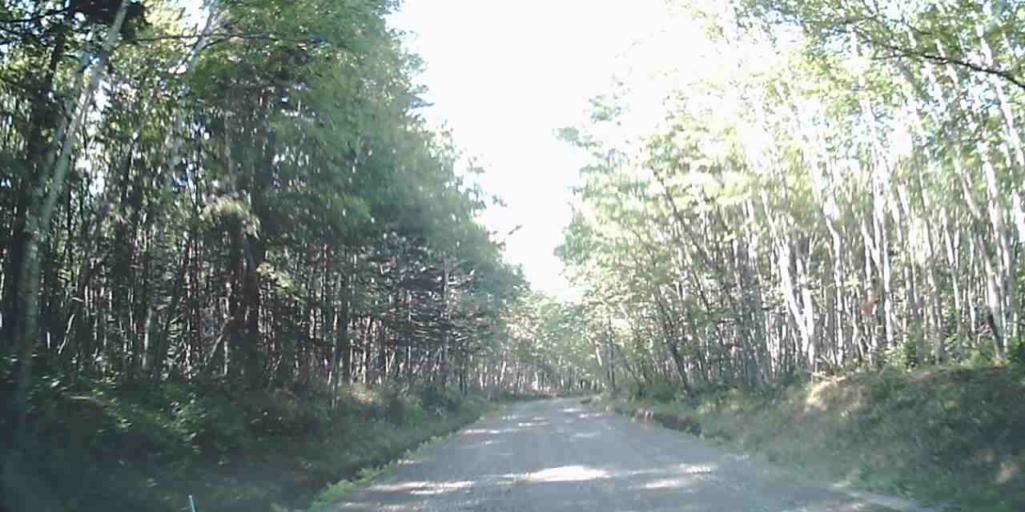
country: JP
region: Hokkaido
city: Shiraoi
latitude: 42.7087
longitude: 141.3983
